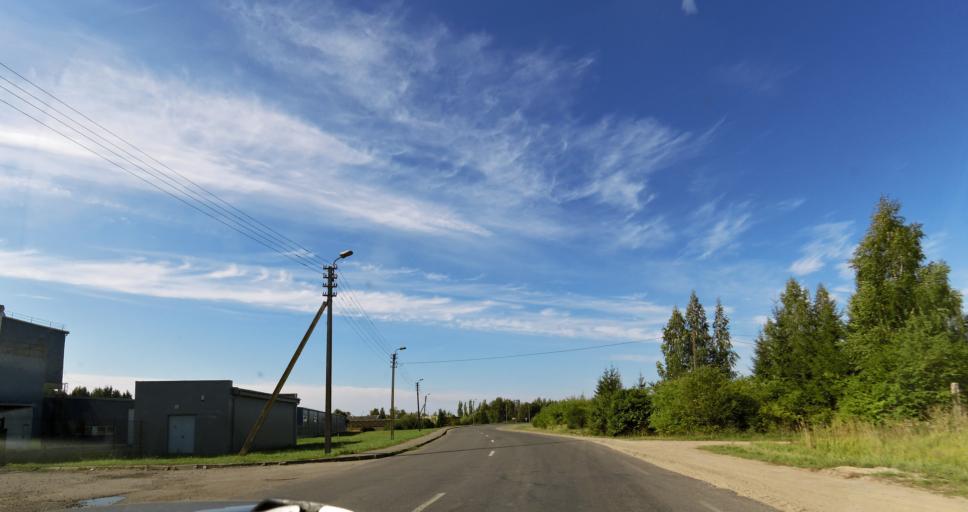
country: LT
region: Panevezys
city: Pasvalys
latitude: 56.0704
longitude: 24.4042
